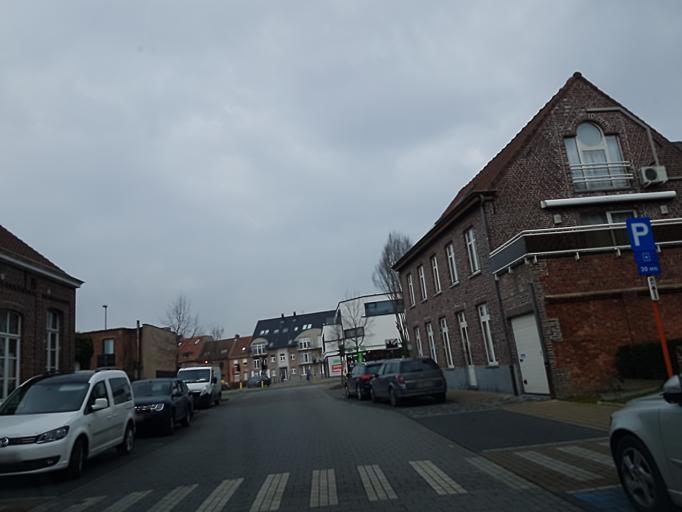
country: BE
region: Flanders
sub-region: Provincie Oost-Vlaanderen
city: Deinze
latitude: 50.9833
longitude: 3.5609
